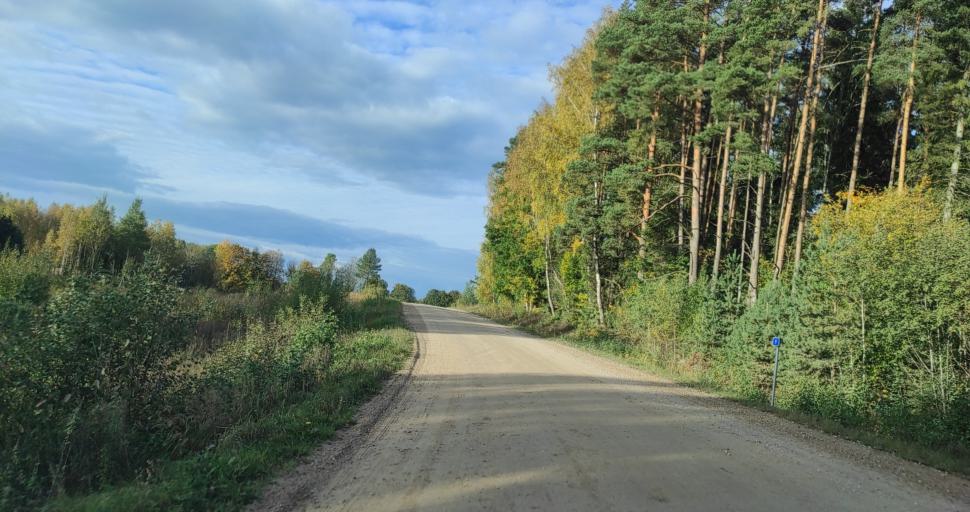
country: LV
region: Skrunda
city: Skrunda
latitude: 56.7435
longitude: 21.8576
